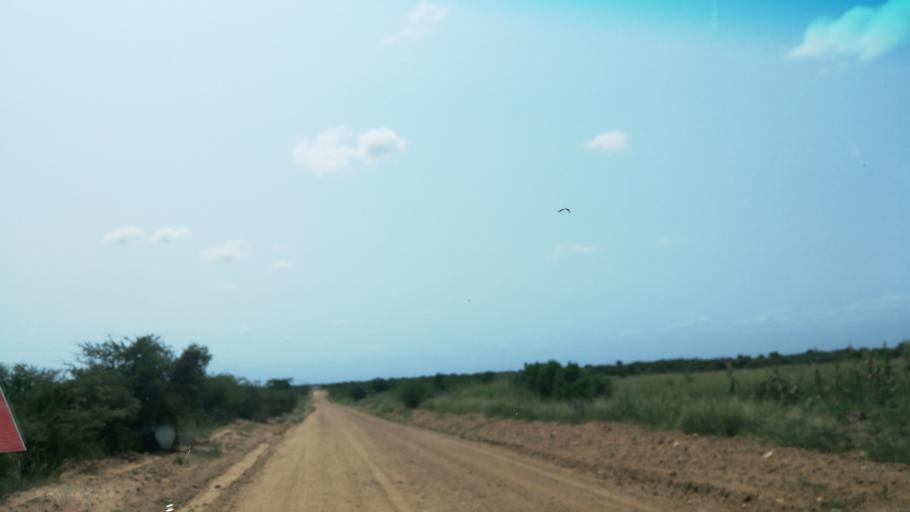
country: MZ
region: Maputo
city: Matola
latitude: -26.0820
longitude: 32.3914
